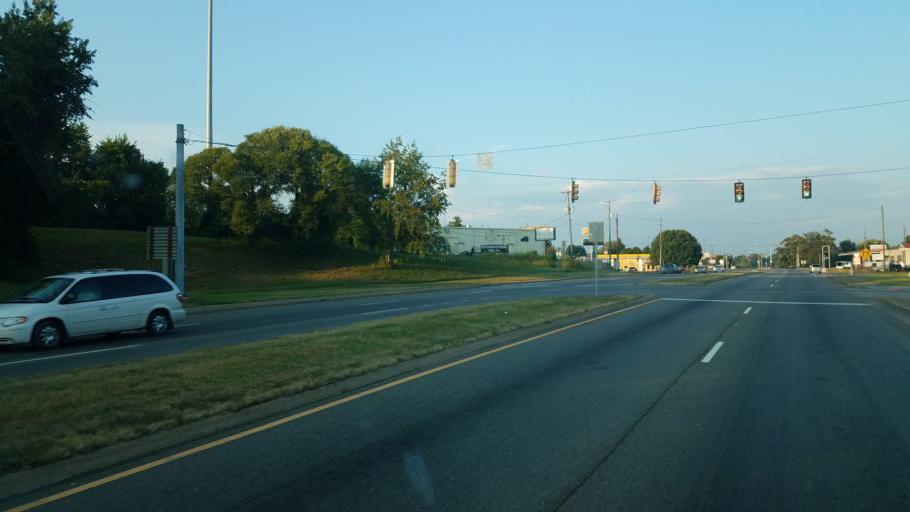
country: US
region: Tennessee
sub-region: Sullivan County
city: Kingsport
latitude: 36.5569
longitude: -82.5806
